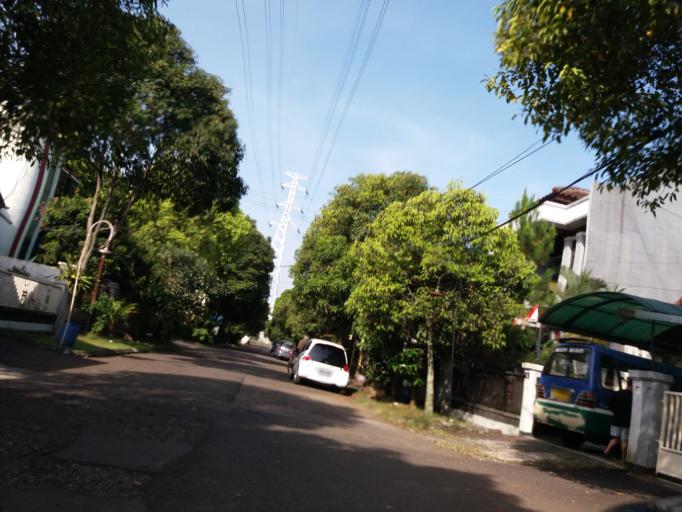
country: ID
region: West Java
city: Pameungpeuk
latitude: -6.9639
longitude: 107.6315
